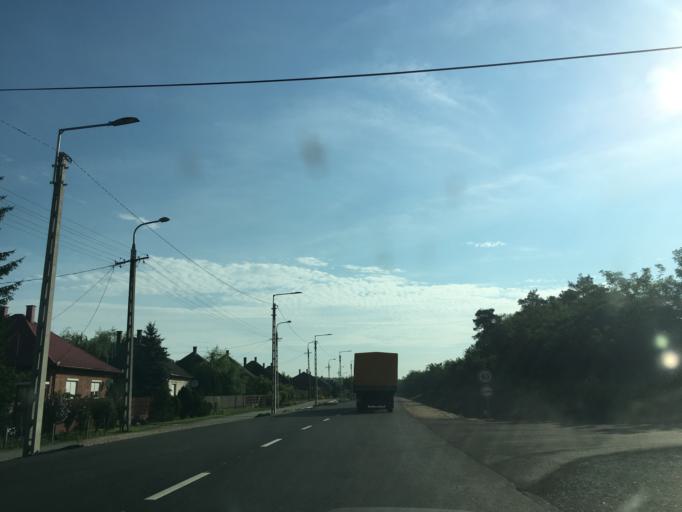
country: HU
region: Hajdu-Bihar
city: Nyiradony
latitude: 47.6629
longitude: 21.8417
